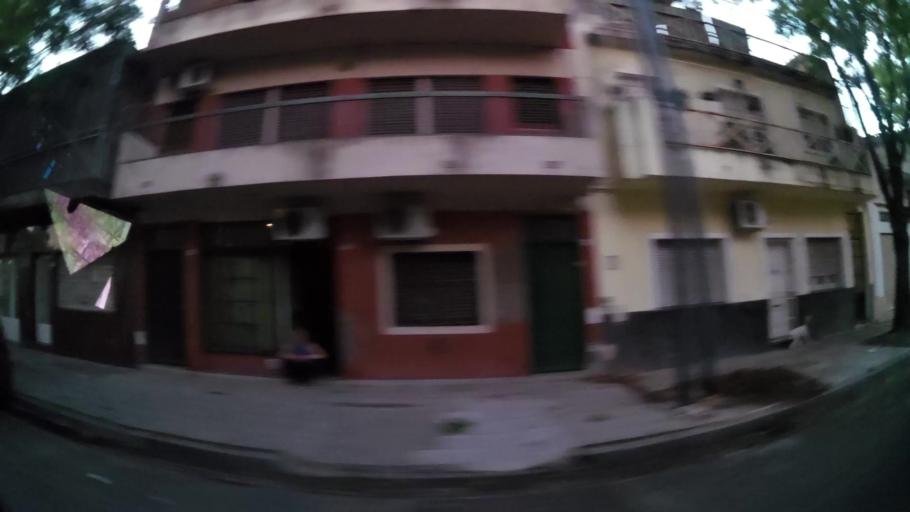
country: AR
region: Buenos Aires F.D.
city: Villa Santa Rita
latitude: -34.6373
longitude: -58.4365
